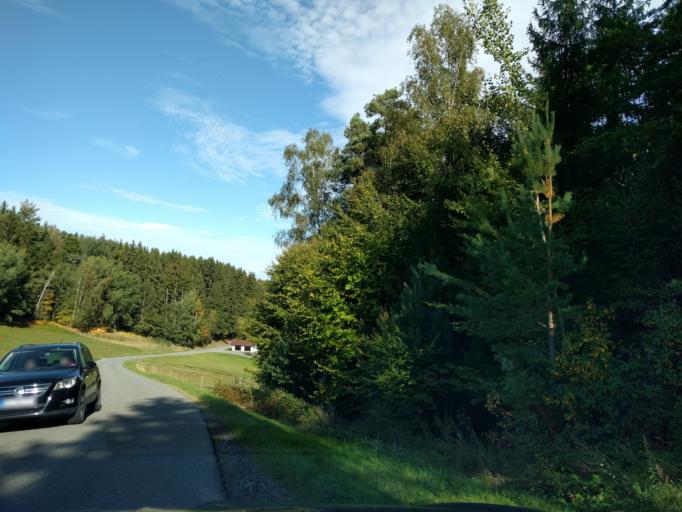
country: DE
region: Bavaria
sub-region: Upper Palatinate
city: Kotzting
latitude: 49.1502
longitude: 12.8909
